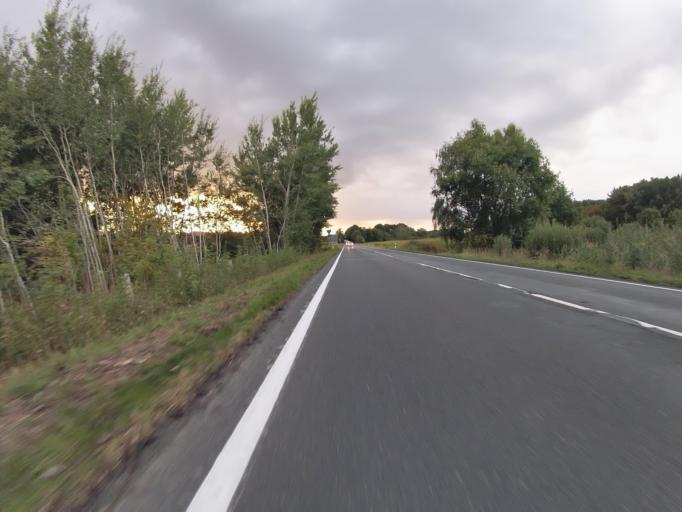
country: DE
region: North Rhine-Westphalia
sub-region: Regierungsbezirk Munster
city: Westerkappeln
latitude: 52.2797
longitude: 7.8620
